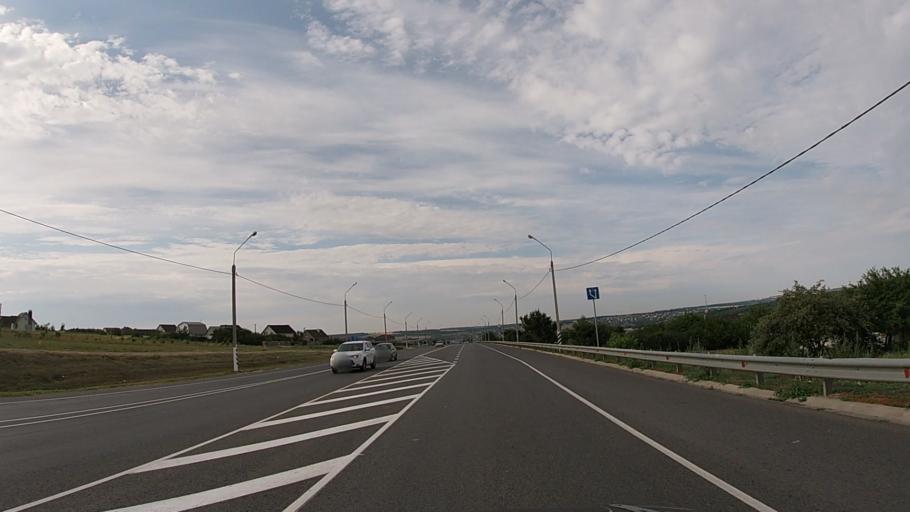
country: RU
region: Belgorod
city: Severnyy
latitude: 50.6506
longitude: 36.4676
